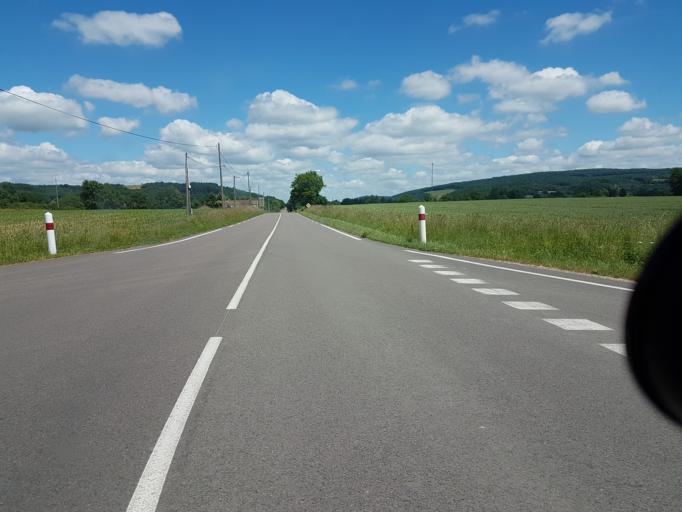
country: FR
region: Bourgogne
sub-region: Departement de Saone-et-Loire
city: Curgy
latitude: 47.0504
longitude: 4.3469
